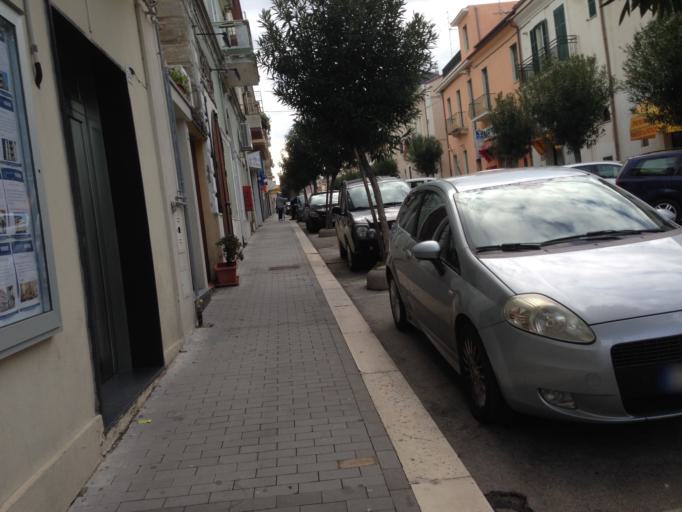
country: IT
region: Molise
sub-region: Provincia di Campobasso
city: Termoli
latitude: 42.0030
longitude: 14.9967
